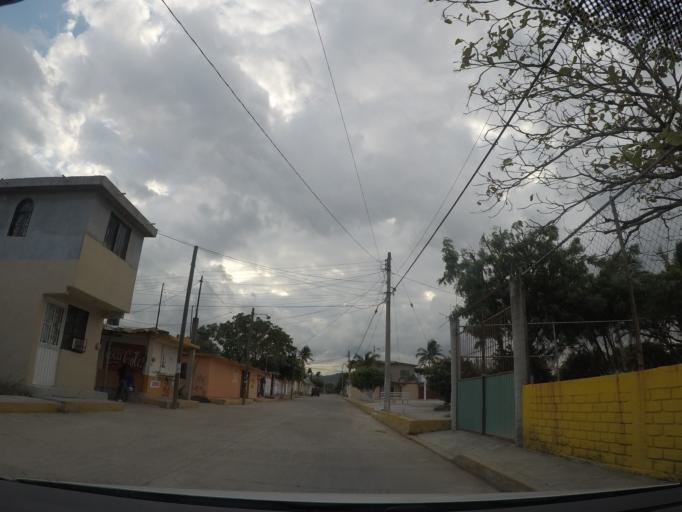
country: MX
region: Oaxaca
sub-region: Salina Cruz
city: Salina Cruz
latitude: 16.2146
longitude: -95.1980
